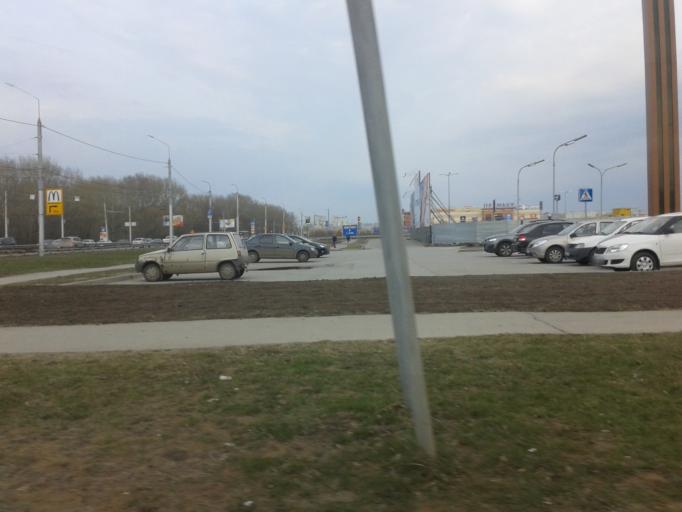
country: RU
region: Rjazan
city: Ryazan'
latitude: 54.6386
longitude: 39.6785
